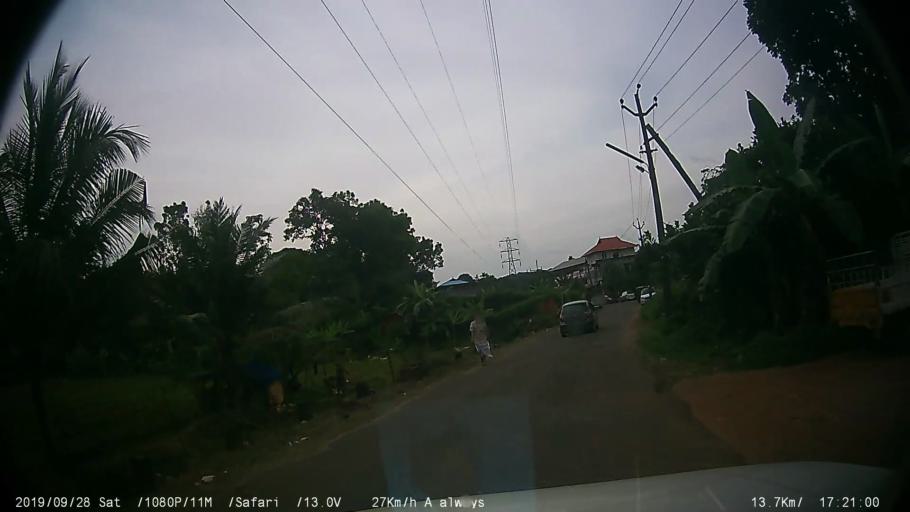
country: IN
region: Kerala
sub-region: Kottayam
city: Palackattumala
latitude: 9.7558
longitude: 76.5602
